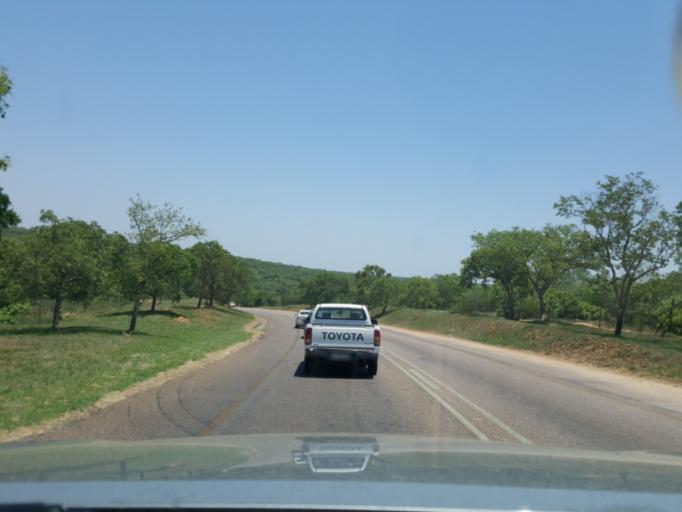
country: ZA
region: Limpopo
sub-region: Mopani District Municipality
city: Hoedspruit
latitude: -24.5471
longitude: 31.0388
